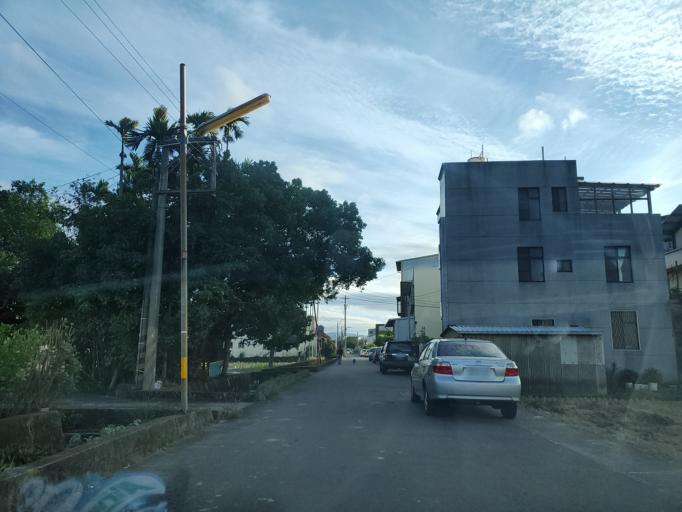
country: TW
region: Taiwan
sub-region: Miaoli
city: Miaoli
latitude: 24.5581
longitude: 120.8300
